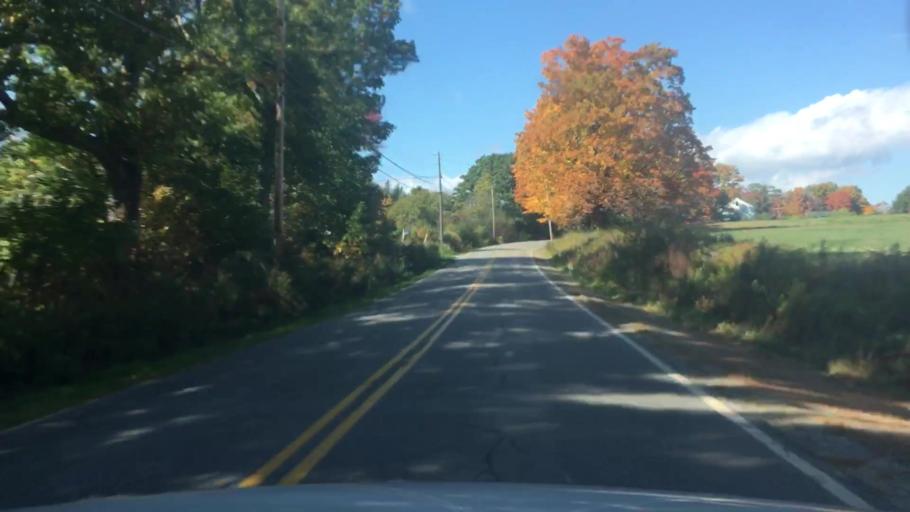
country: US
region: Maine
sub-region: Knox County
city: Thomaston
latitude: 44.0904
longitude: -69.2151
